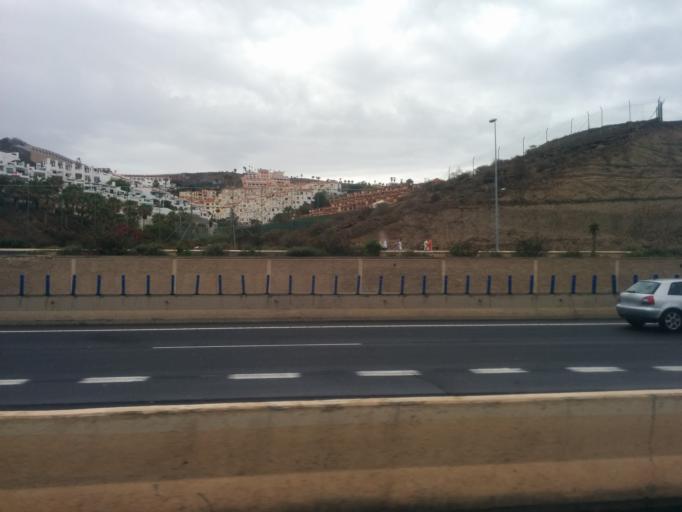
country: ES
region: Canary Islands
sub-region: Provincia de Santa Cruz de Tenerife
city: Playa de las Americas
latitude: 28.0844
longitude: -16.7291
